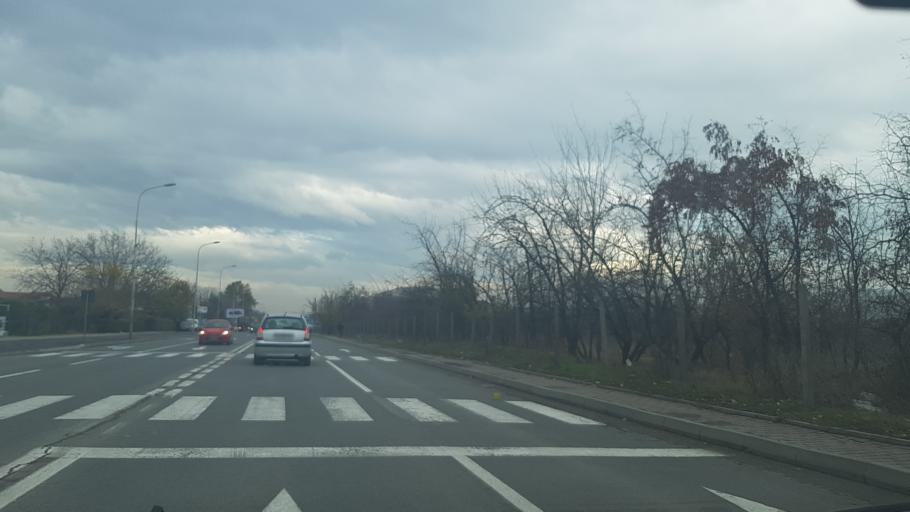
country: MK
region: Kisela Voda
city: Usje
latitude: 41.9768
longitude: 21.4501
